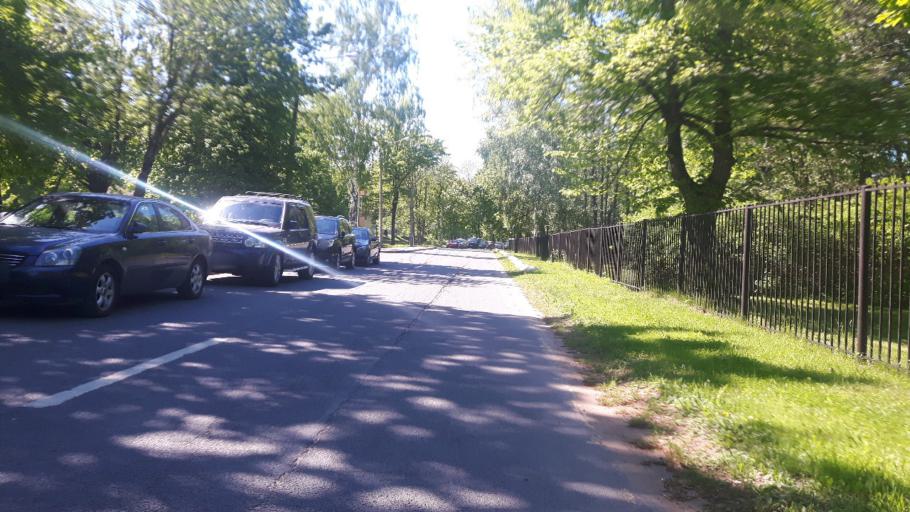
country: RU
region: St.-Petersburg
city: Peterhof
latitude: 59.8810
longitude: 29.9229
